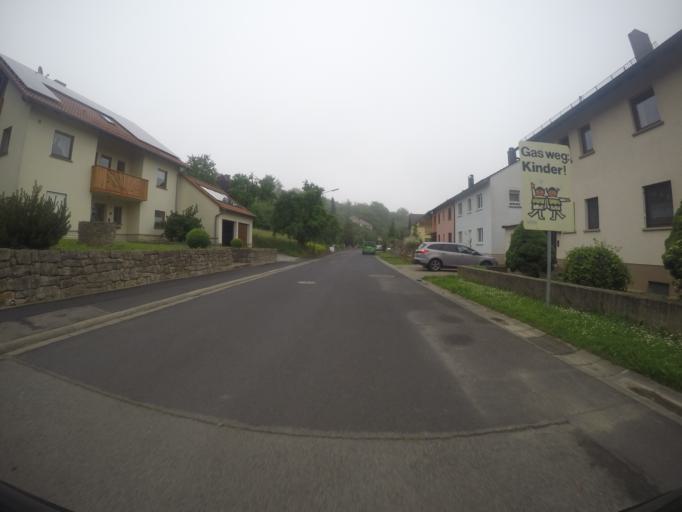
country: DE
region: Bavaria
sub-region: Regierungsbezirk Unterfranken
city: Schwanfeld
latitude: 49.9208
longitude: 10.1481
